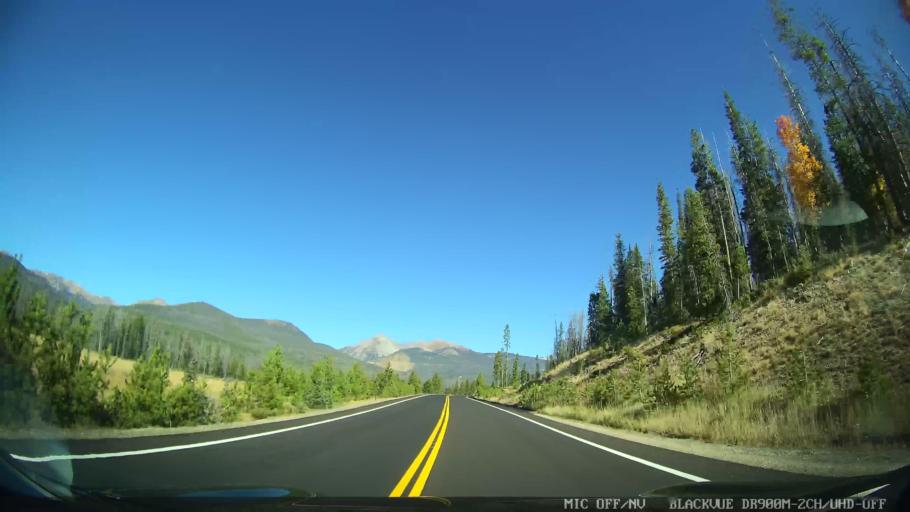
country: US
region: Colorado
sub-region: Grand County
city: Granby
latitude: 40.3288
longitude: -105.8537
